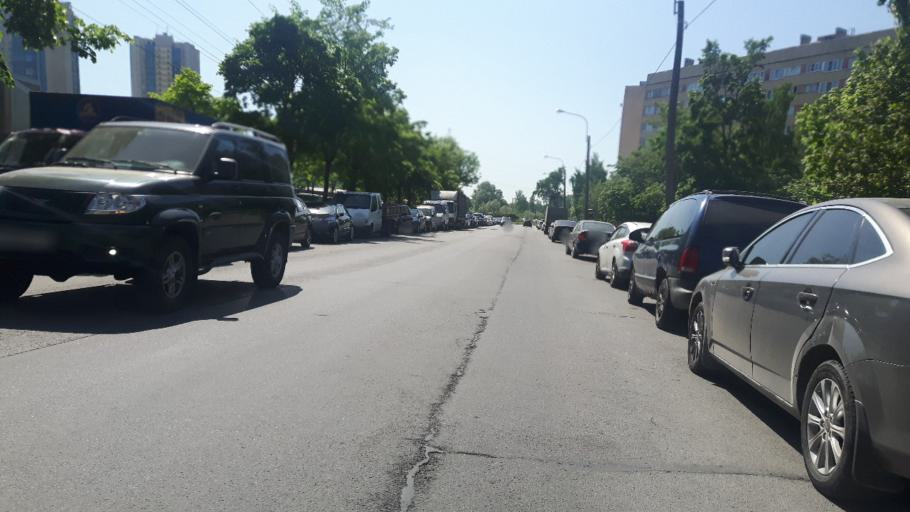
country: RU
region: St.-Petersburg
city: Uritsk
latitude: 59.8481
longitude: 30.2130
